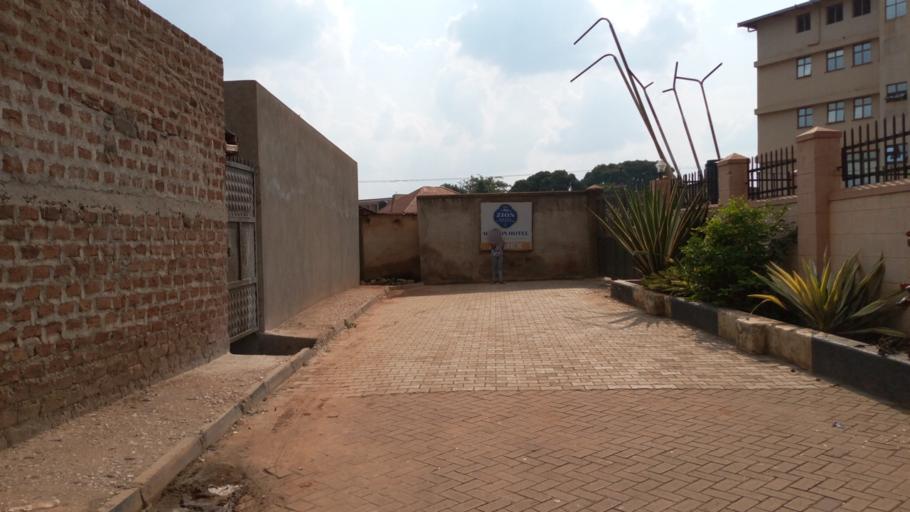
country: UG
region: Central Region
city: Kampala Central Division
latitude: 0.3267
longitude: 32.5658
